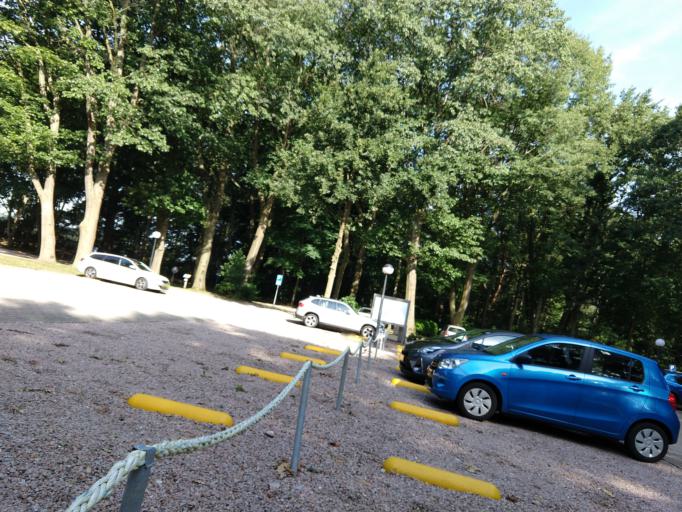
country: NL
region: Gelderland
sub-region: Gemeente Ede
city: Lunteren
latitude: 52.0755
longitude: 5.6487
